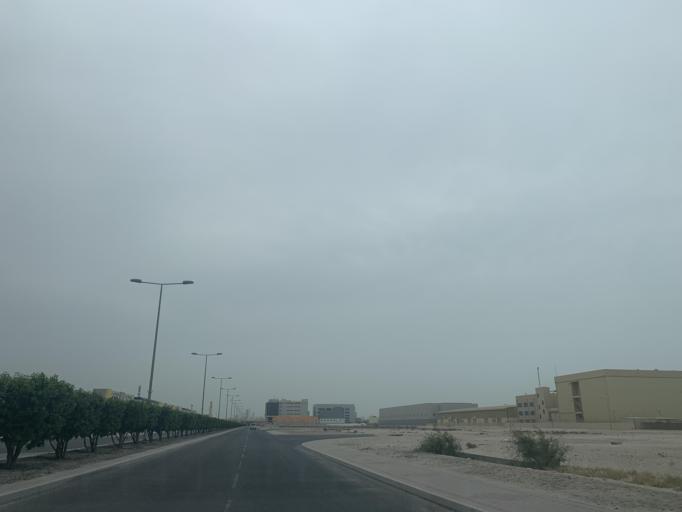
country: BH
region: Muharraq
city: Al Hadd
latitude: 26.2134
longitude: 50.6789
